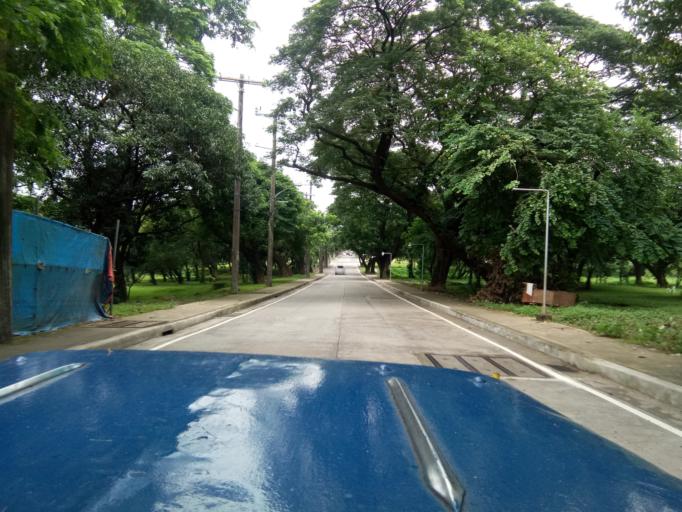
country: PH
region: Metro Manila
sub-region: Quezon City
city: Quezon City
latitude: 14.6530
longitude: 121.0626
